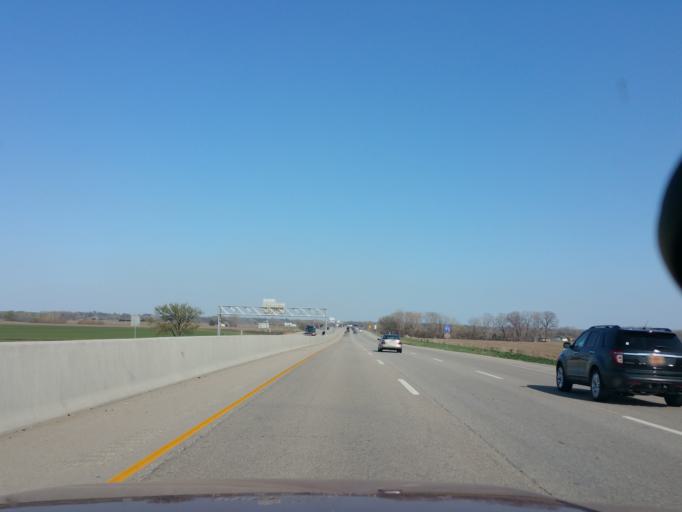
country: US
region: Kansas
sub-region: Douglas County
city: Lawrence
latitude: 38.9938
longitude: -95.2228
